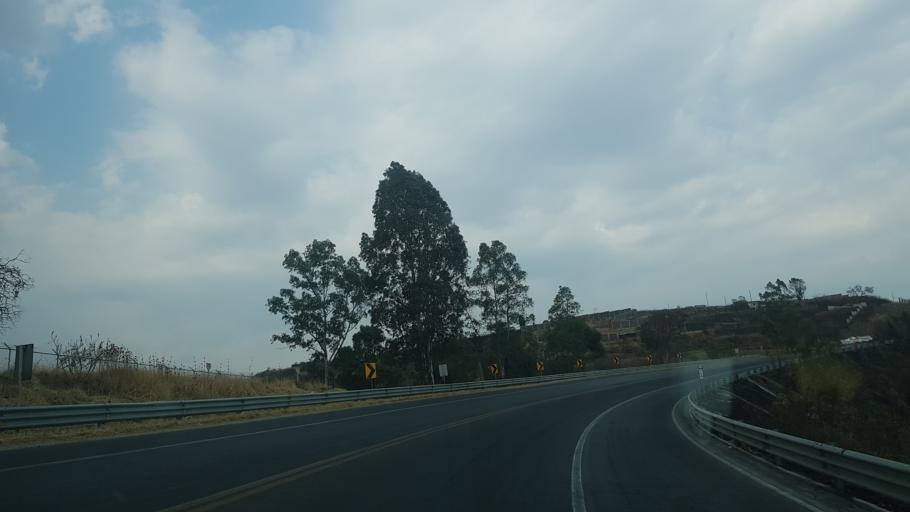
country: MX
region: Puebla
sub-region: Santa Isabel Cholula
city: San Martin Tlamapa
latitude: 18.9752
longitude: -98.3800
